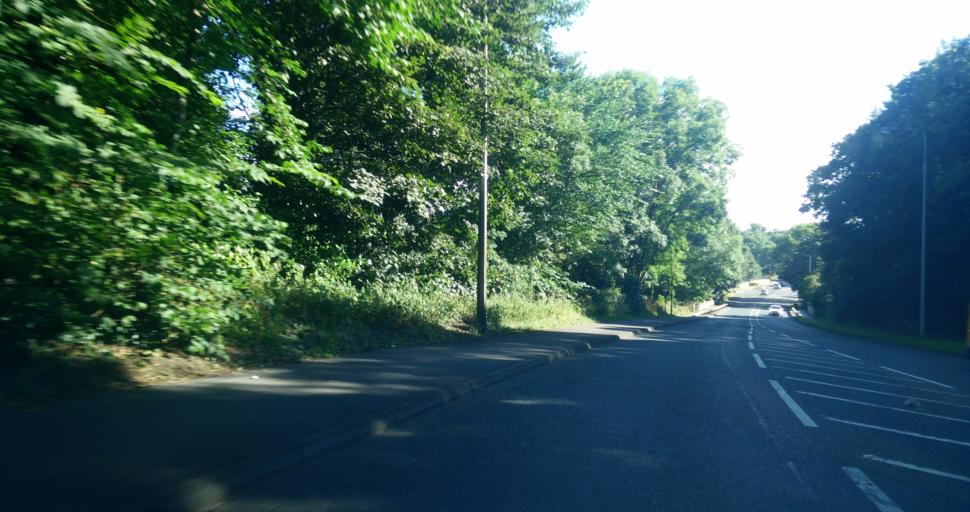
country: GB
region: England
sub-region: County Durham
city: Durham
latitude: 54.7394
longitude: -1.5872
